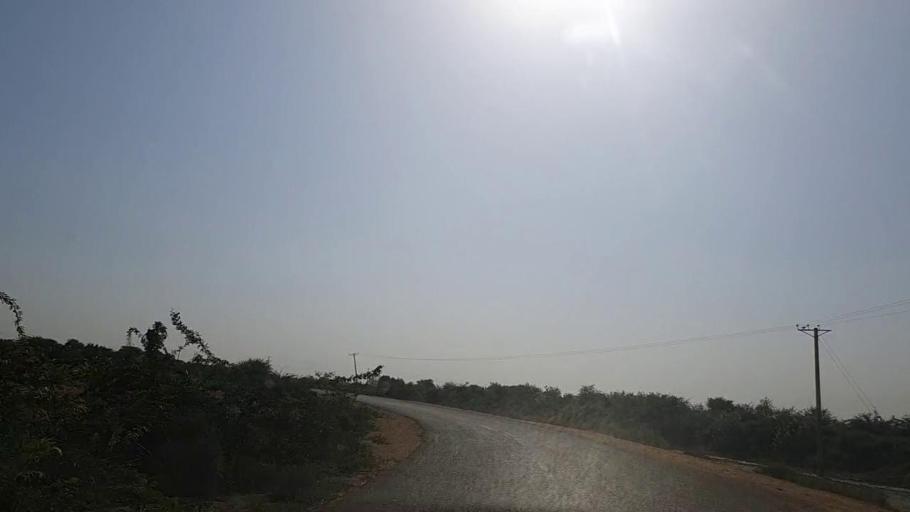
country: PK
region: Sindh
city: Jati
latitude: 24.4574
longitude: 68.2653
